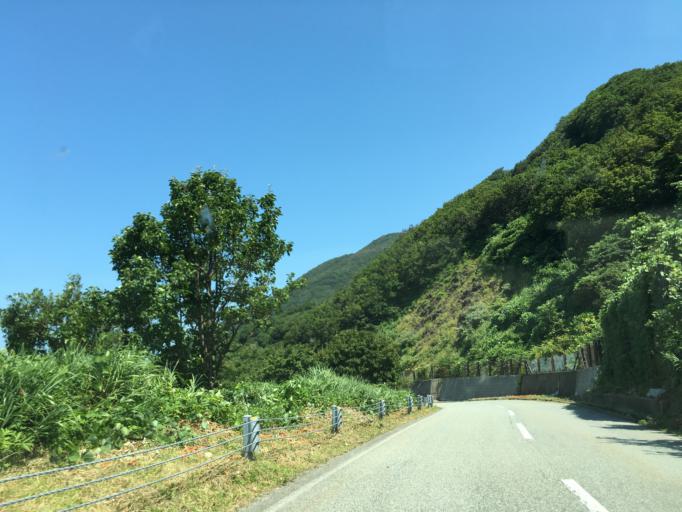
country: JP
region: Akita
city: Tenno
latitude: 39.8864
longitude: 139.7411
